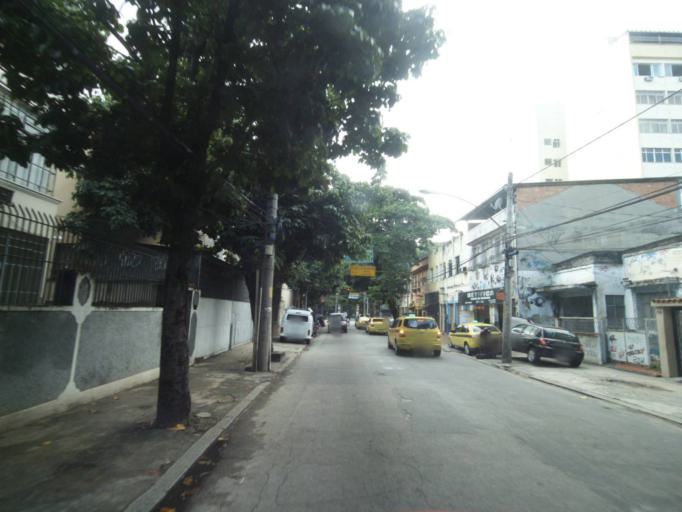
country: BR
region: Rio de Janeiro
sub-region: Rio De Janeiro
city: Rio de Janeiro
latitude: -22.9177
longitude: -43.2599
